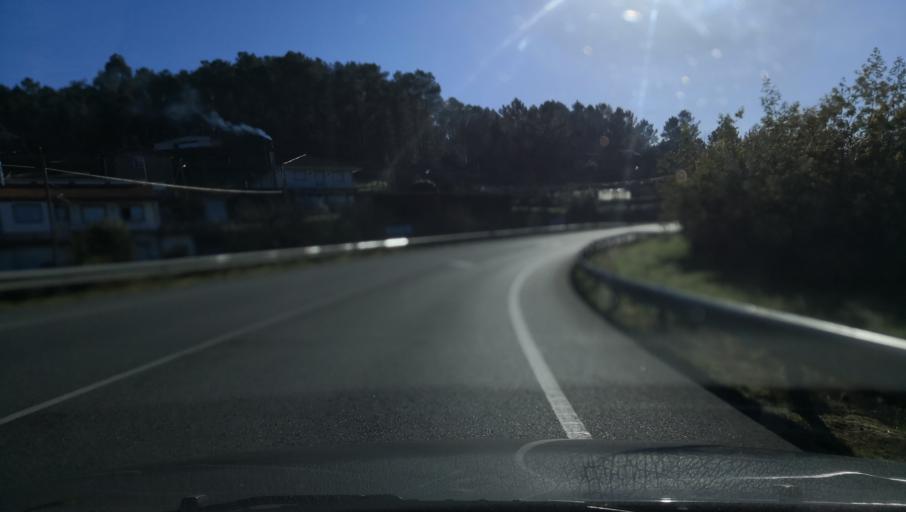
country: ES
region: Galicia
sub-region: Provincia da Coruna
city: Ribeira
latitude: 42.7587
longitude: -8.3961
